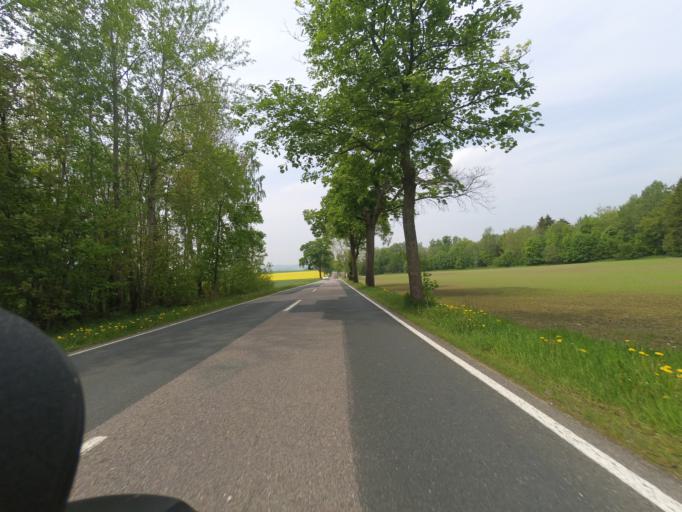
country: DE
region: Saxony
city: Grossruckerswalde
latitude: 50.6471
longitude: 13.1056
